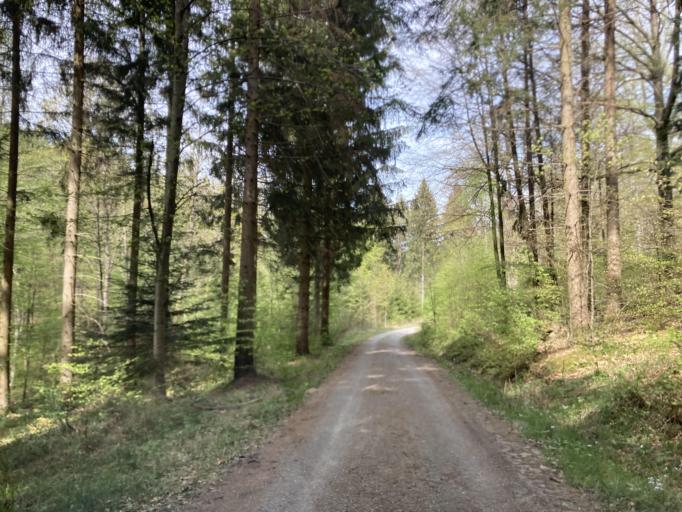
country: DE
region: Baden-Wuerttemberg
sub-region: Tuebingen Region
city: Rottenburg
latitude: 48.4569
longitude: 8.9860
